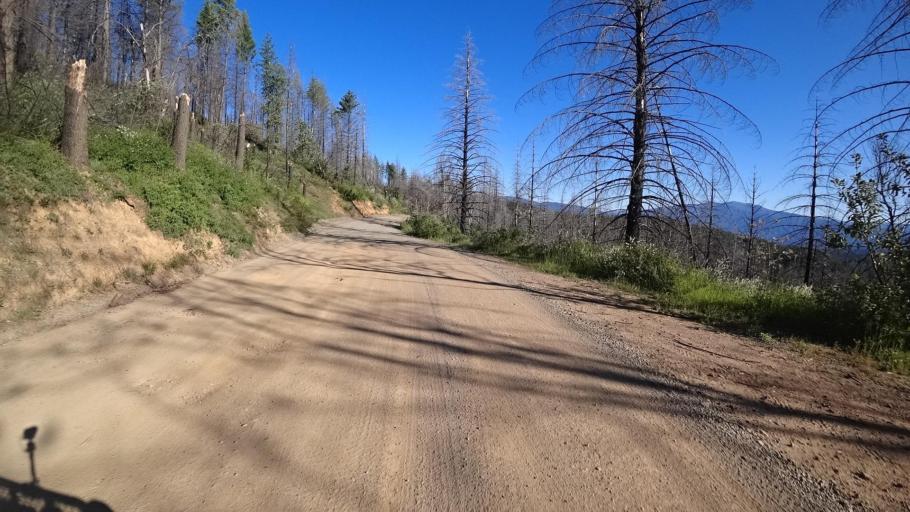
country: US
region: California
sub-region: Lake County
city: Upper Lake
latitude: 39.3404
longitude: -122.9589
